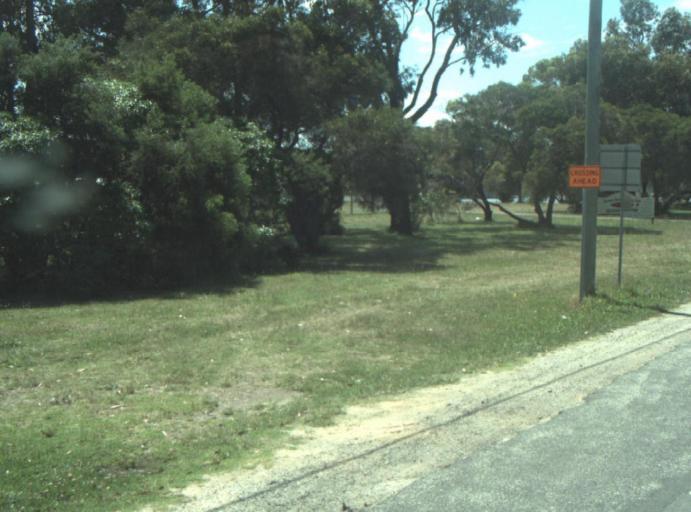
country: AU
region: Victoria
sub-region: Greater Geelong
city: Leopold
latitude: -38.2745
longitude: 144.4890
